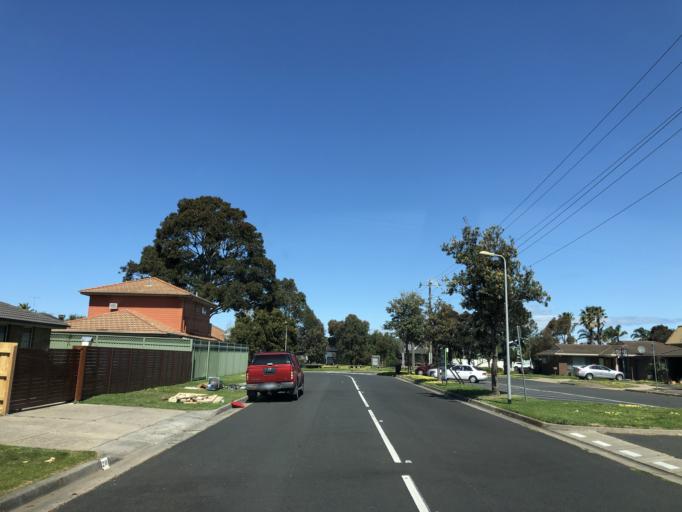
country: AU
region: Victoria
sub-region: Kingston
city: Patterson Lakes
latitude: -38.0784
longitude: 145.1454
